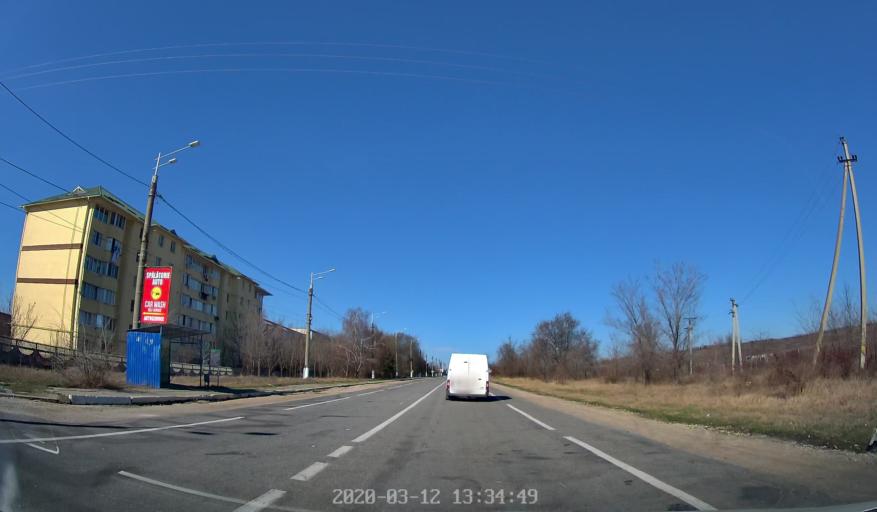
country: MD
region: Laloveni
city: Ialoveni
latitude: 46.9666
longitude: 28.7668
